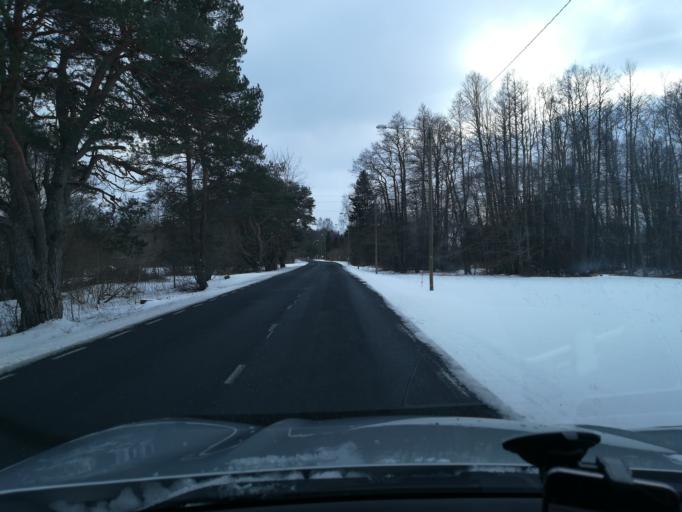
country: EE
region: Harju
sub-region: Keila linn
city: Keila
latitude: 59.3939
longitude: 24.4127
